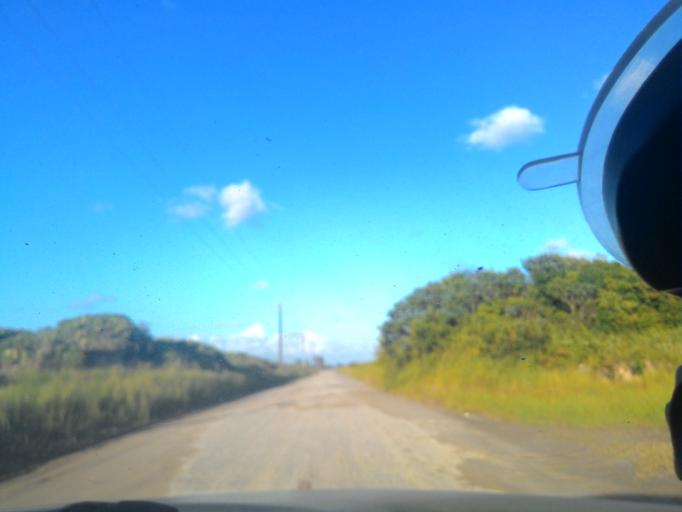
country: BR
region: Sao Paulo
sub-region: Pariquera-Acu
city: Pariquera Acu
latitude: -24.8752
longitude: -47.7284
